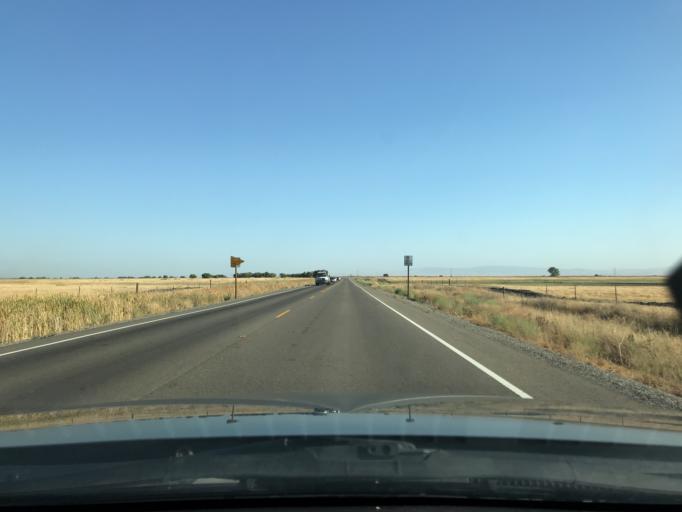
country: US
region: California
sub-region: Merced County
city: Gustine
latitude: 37.2239
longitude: -120.8521
